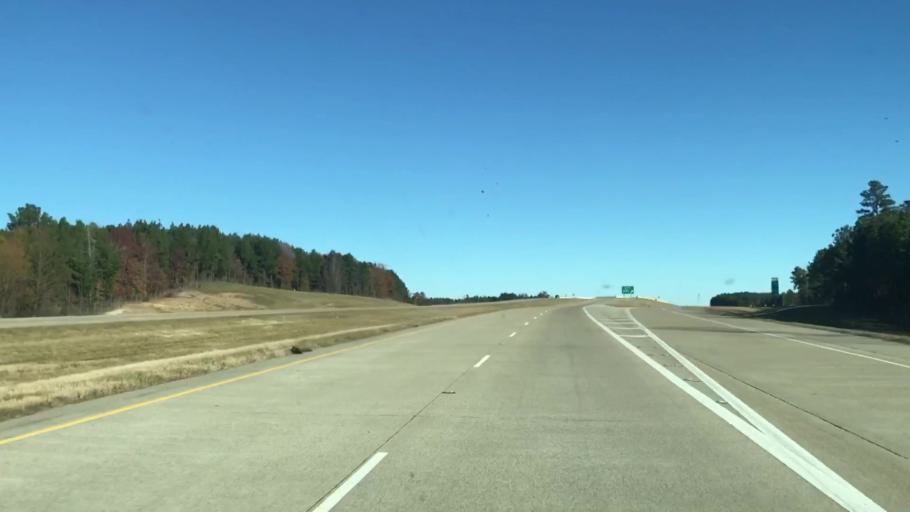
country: US
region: Louisiana
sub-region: Caddo Parish
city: Oil City
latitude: 32.8098
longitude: -93.8846
